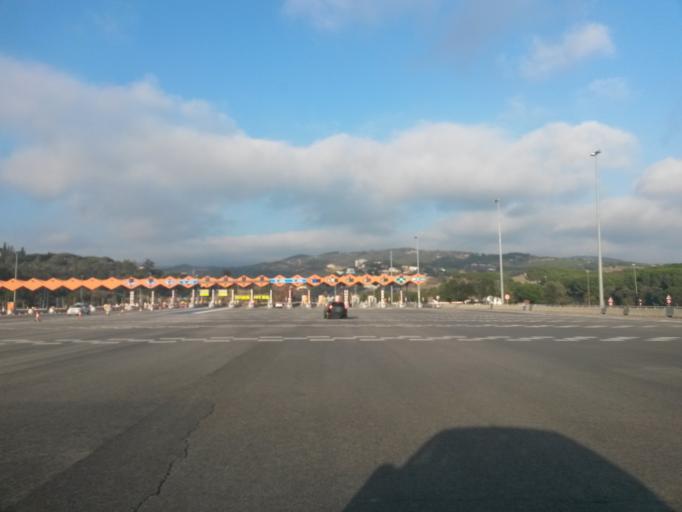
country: ES
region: Catalonia
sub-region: Provincia de Barcelona
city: Arenys de Mar
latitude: 41.5861
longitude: 2.5384
